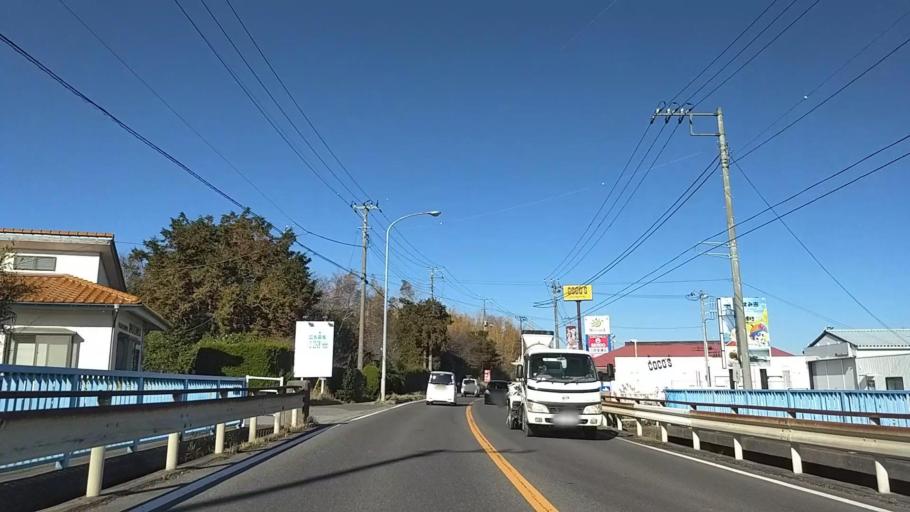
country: JP
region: Chiba
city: Ohara
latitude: 35.2872
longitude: 140.3920
